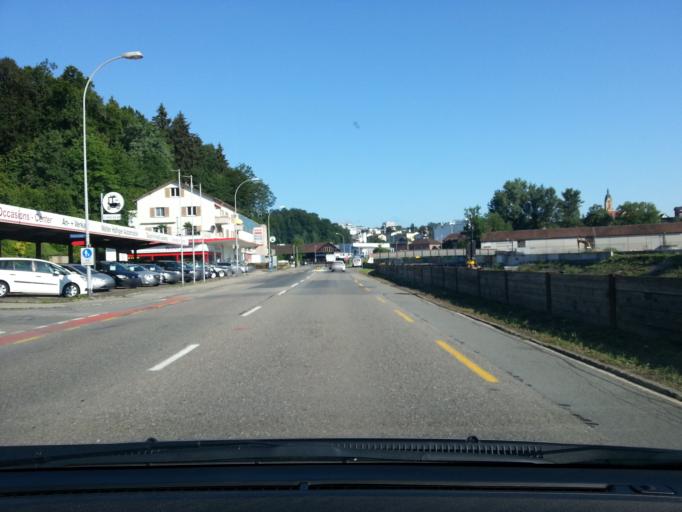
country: CH
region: Lucerne
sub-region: Hochdorf District
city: Emmen
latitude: 47.0703
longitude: 8.2770
